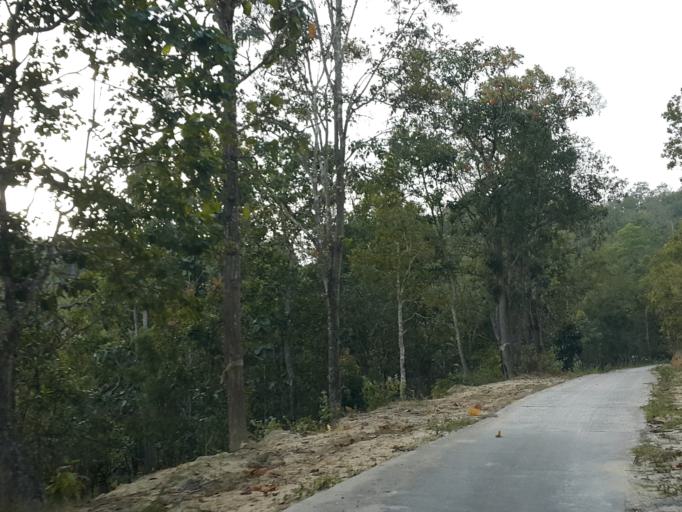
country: TH
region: Chiang Mai
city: Om Koi
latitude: 17.8016
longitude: 98.3173
